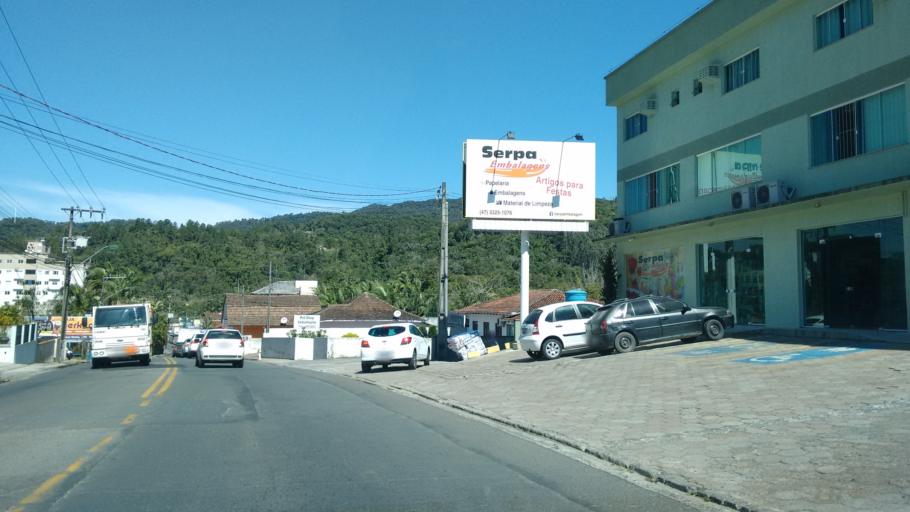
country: BR
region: Santa Catarina
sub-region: Blumenau
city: Blumenau
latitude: -26.9205
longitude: -49.1063
